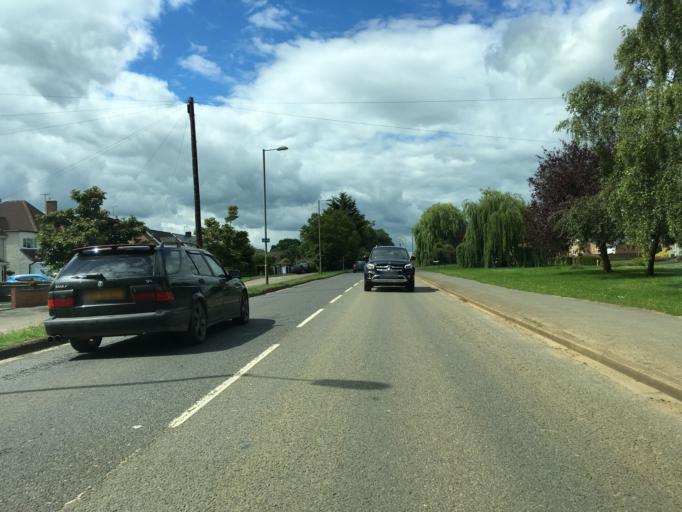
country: GB
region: England
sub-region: Oxfordshire
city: Banbury
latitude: 52.0501
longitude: -1.3493
